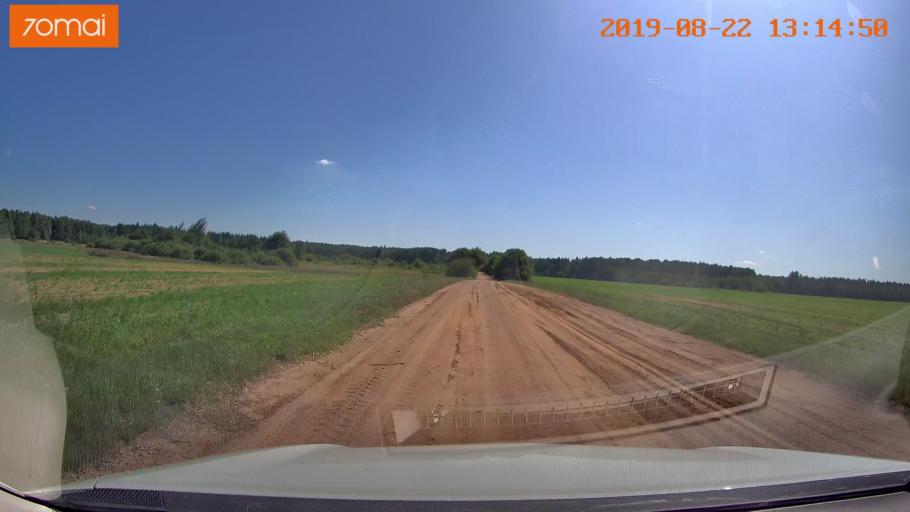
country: BY
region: Minsk
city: Prawdzinski
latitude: 53.2647
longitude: 27.8911
